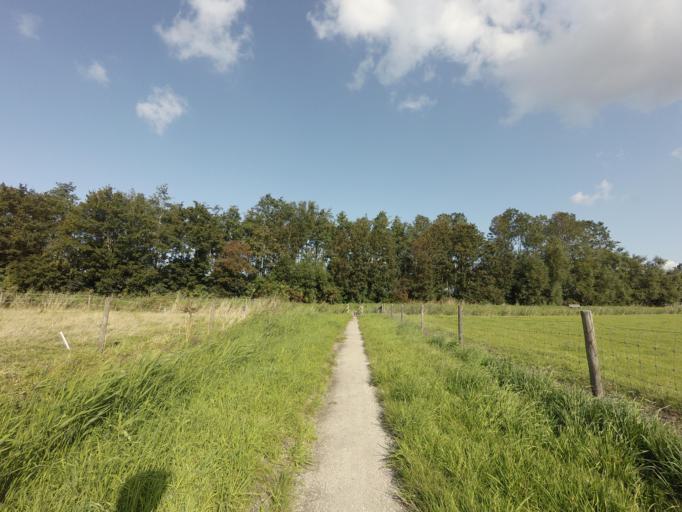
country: NL
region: Friesland
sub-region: Gemeente Franekeradeel
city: Tzummarum
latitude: 53.2385
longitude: 5.5385
